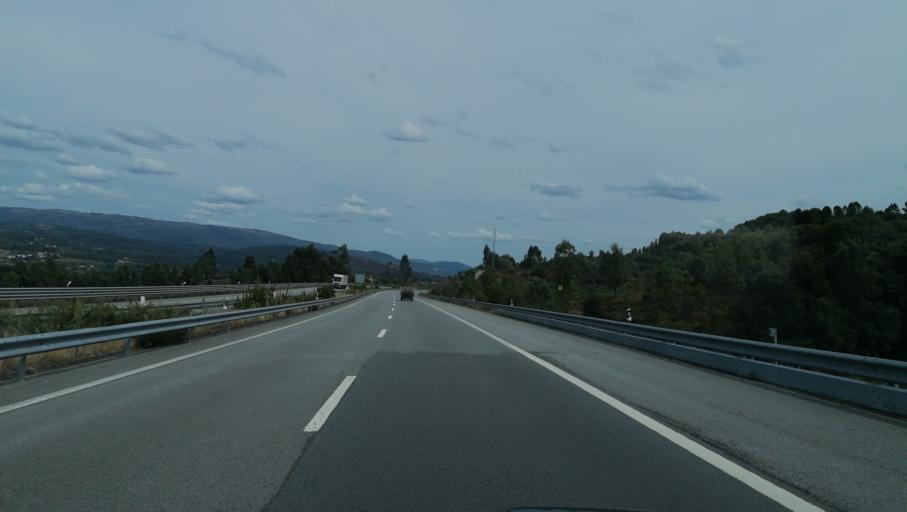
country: PT
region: Braga
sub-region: Cabeceiras de Basto
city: Cabeceiras de Basto
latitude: 41.4722
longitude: -7.9689
